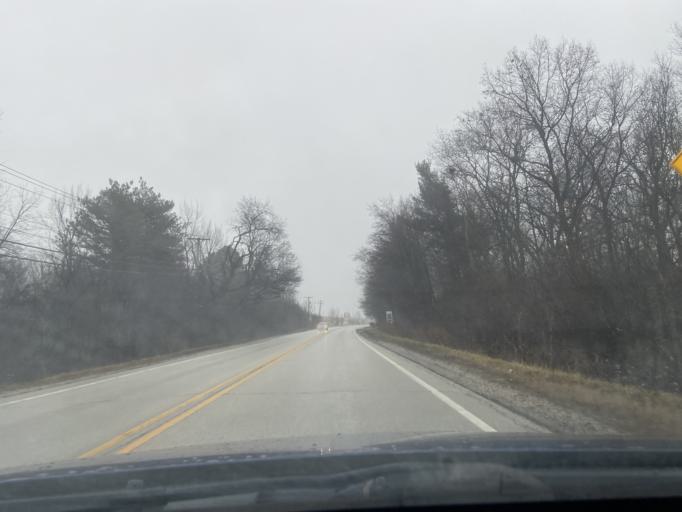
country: US
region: Illinois
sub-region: Lake County
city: Mundelein
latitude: 42.2864
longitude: -88.0517
